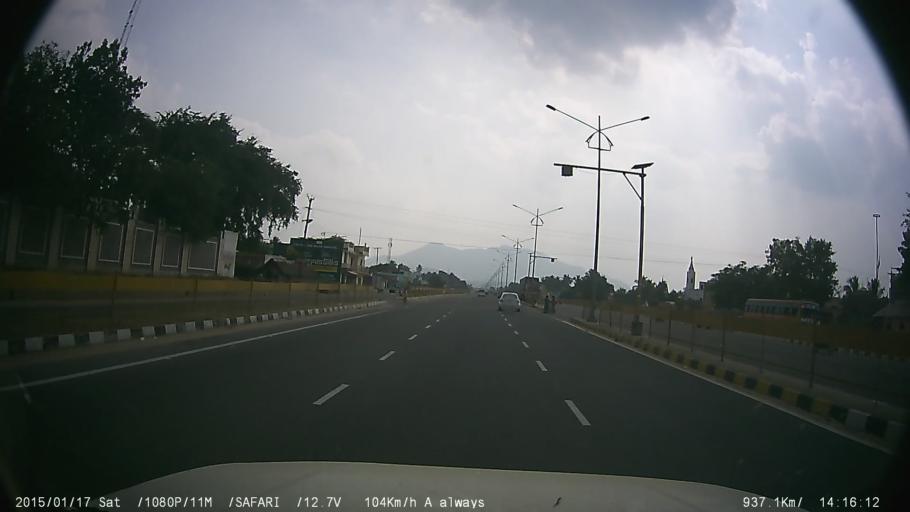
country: IN
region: Tamil Nadu
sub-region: Vellore
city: Ambur
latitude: 12.7583
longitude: 78.7003
